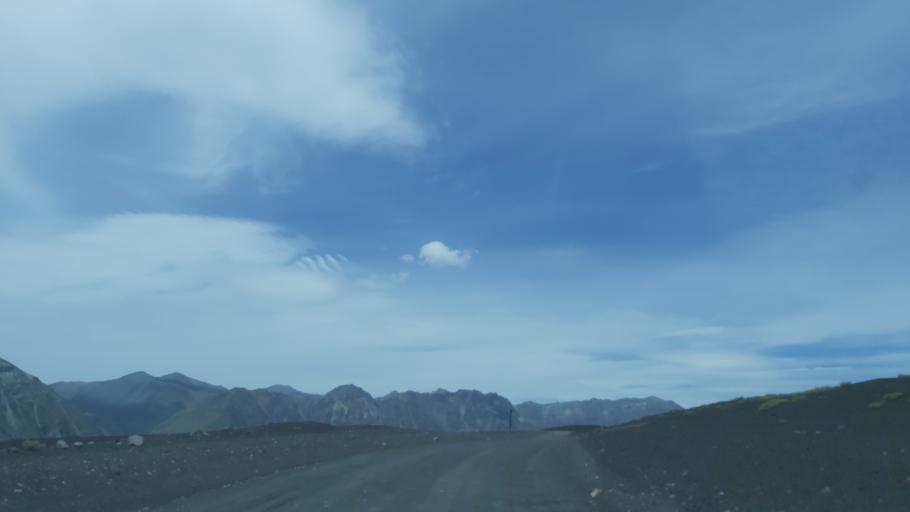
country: AR
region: Neuquen
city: Andacollo
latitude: -37.4113
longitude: -71.2929
